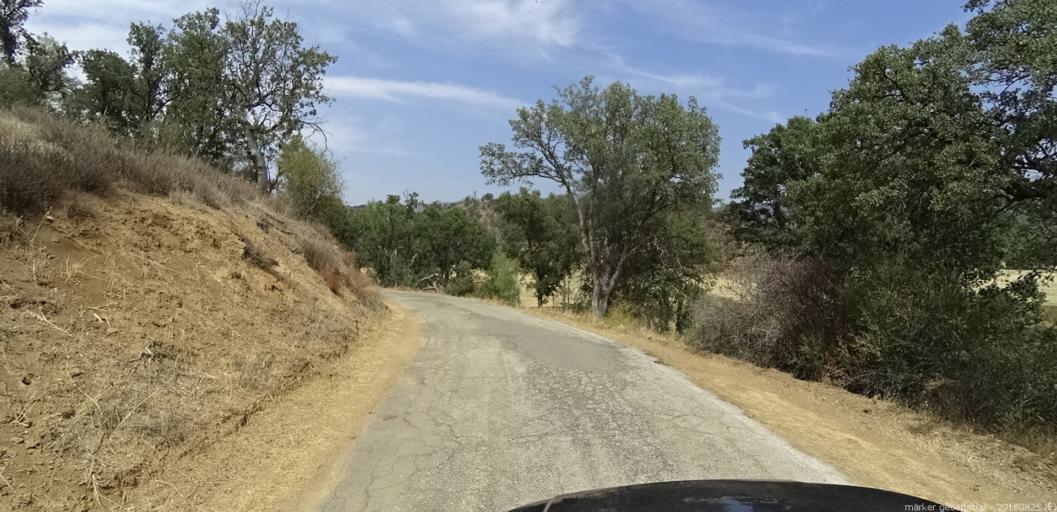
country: US
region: California
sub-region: Fresno County
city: Coalinga
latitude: 36.2212
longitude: -120.7071
